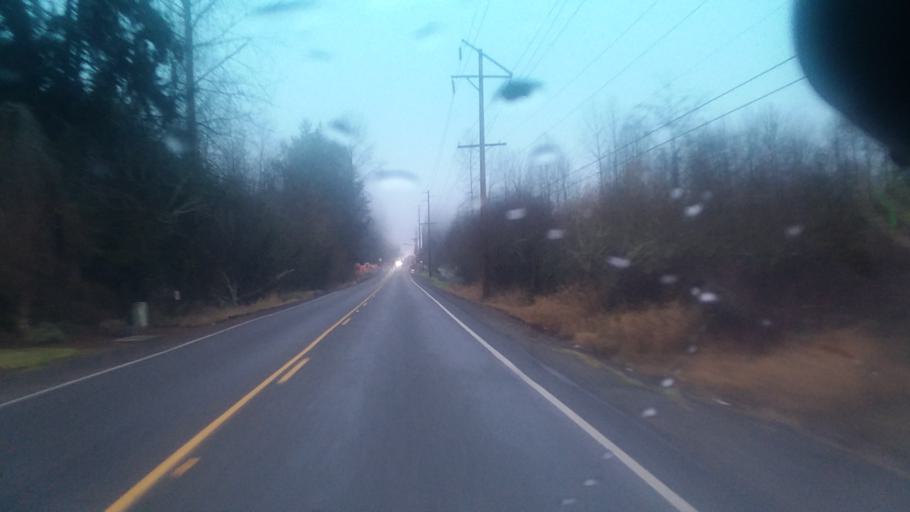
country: US
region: Washington
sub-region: Pierce County
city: South Hill
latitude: 47.1257
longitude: -122.3114
